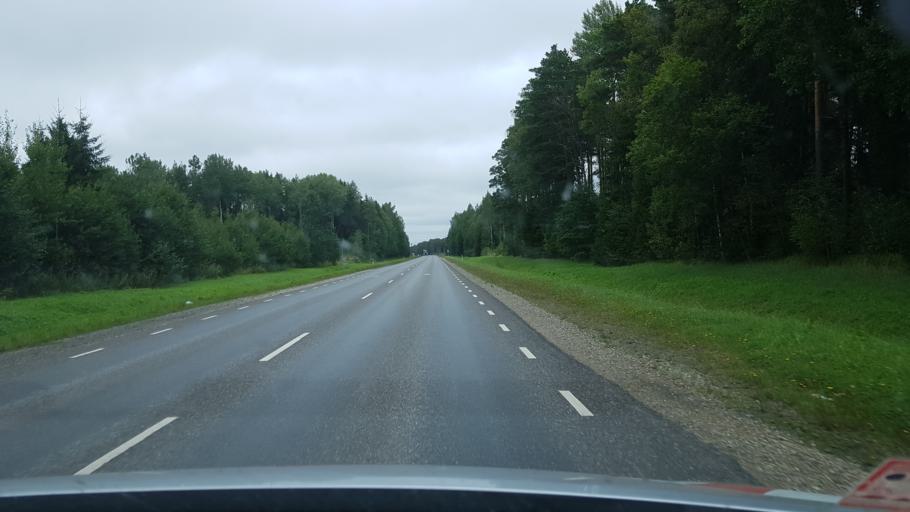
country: EE
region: Viljandimaa
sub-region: Vohma linn
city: Vohma
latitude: 58.5901
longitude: 25.5714
